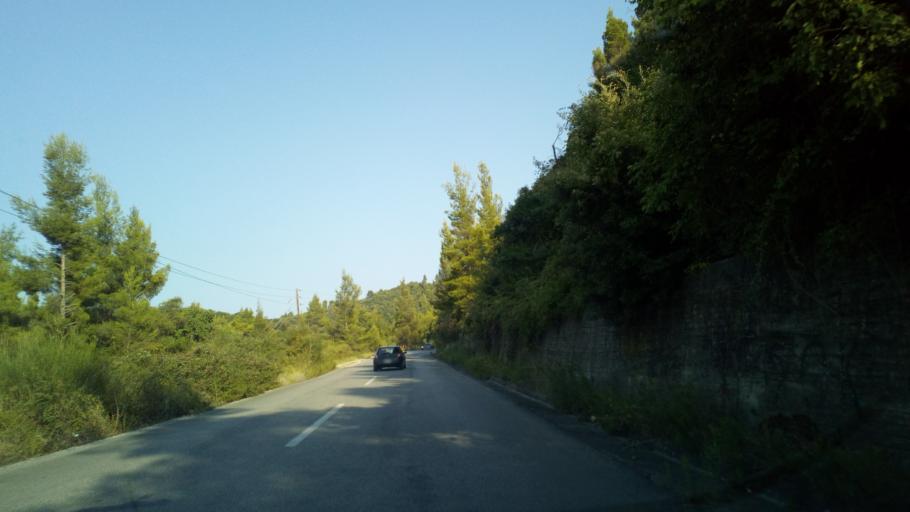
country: GR
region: Central Macedonia
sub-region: Nomos Chalkidikis
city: Neos Marmaras
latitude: 40.1621
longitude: 23.8699
